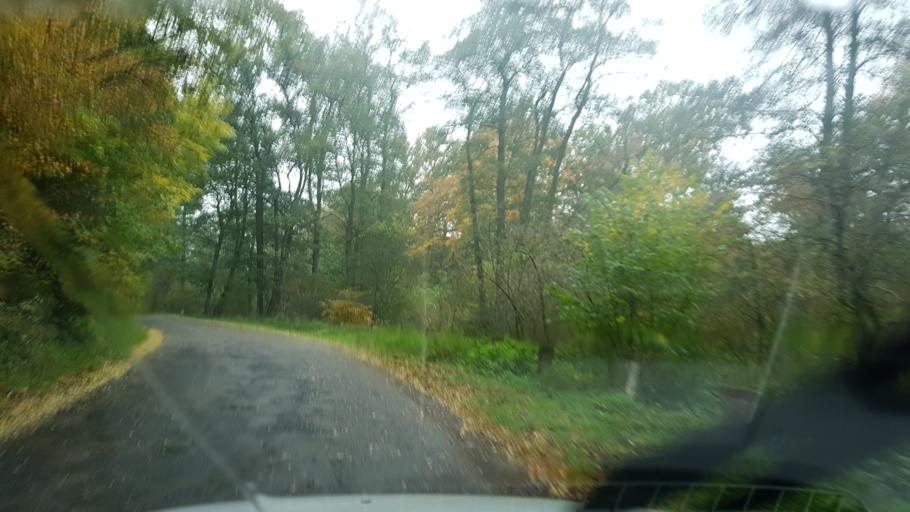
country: PL
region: West Pomeranian Voivodeship
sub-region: Powiat mysliborski
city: Barlinek
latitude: 53.0145
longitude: 15.2233
